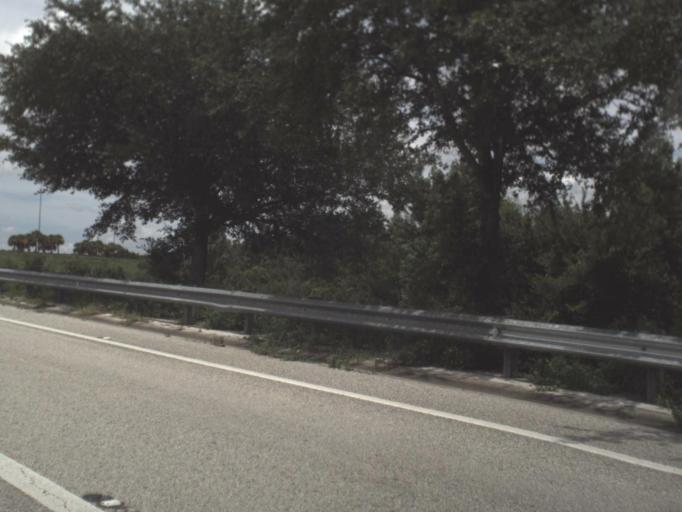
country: US
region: Florida
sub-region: Hillsborough County
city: Pebble Creek
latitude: 28.1928
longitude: -82.3810
